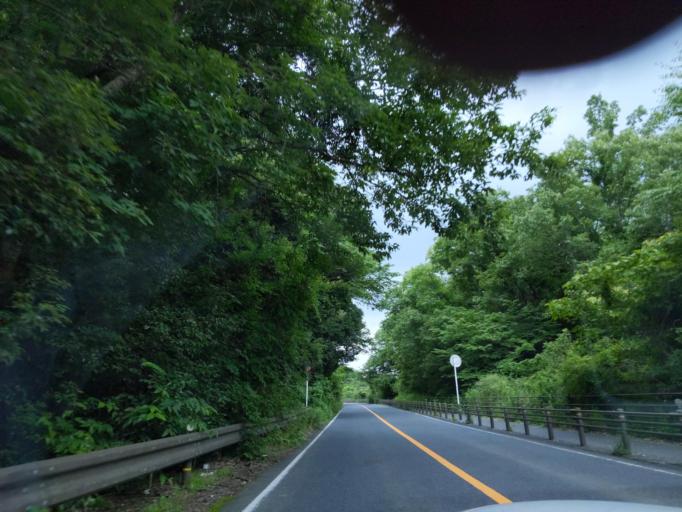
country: JP
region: Aichi
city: Seto
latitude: 35.1888
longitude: 137.1093
